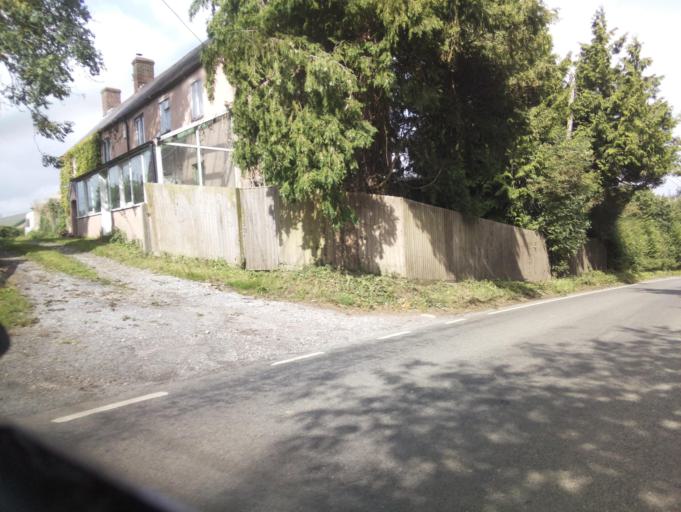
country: GB
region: England
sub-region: Somerset
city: Redlynch
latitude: 51.1044
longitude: -2.4334
